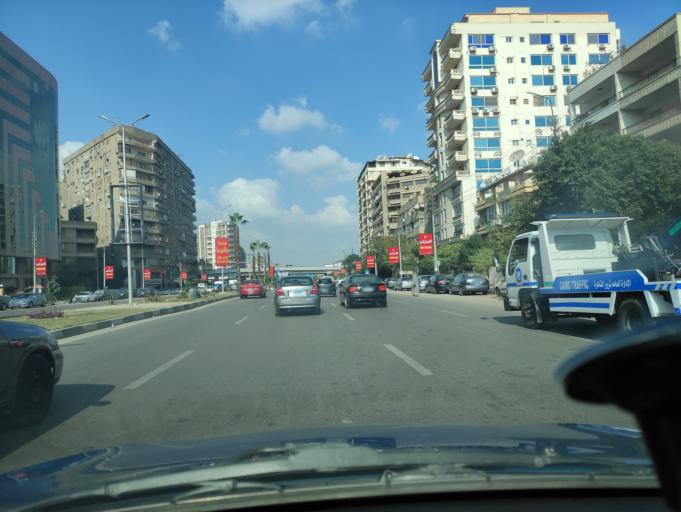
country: EG
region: Muhafazat al Qahirah
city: Cairo
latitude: 30.0885
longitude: 31.3414
